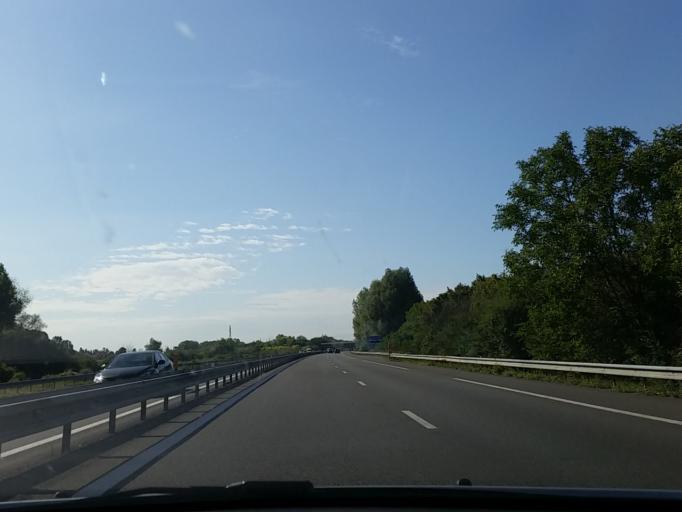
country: FR
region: Centre
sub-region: Departement du Cher
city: Foecy
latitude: 47.1688
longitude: 2.1810
